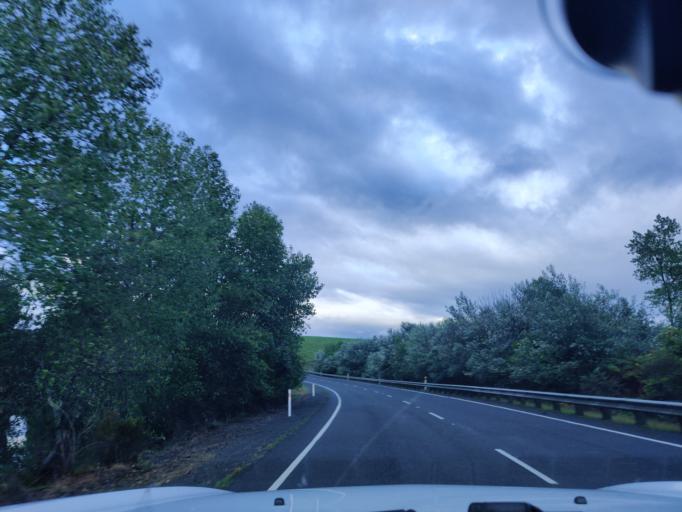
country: NZ
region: Waikato
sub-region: South Waikato District
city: Tokoroa
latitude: -38.3743
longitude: 175.7945
